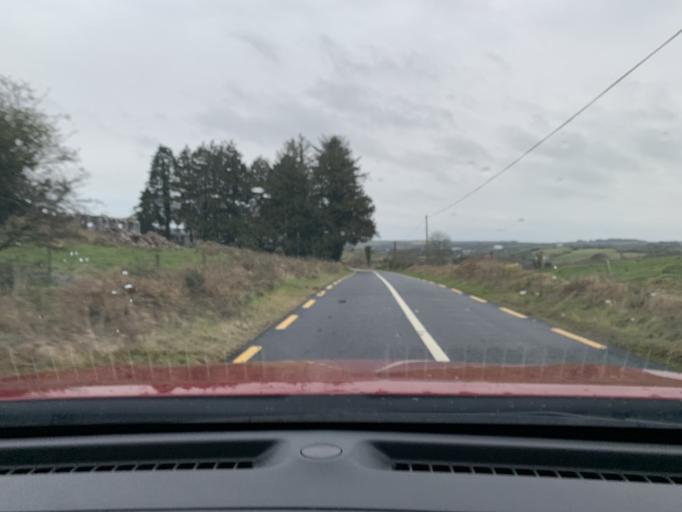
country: IE
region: Connaught
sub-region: Roscommon
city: Boyle
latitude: 53.9790
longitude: -8.3358
